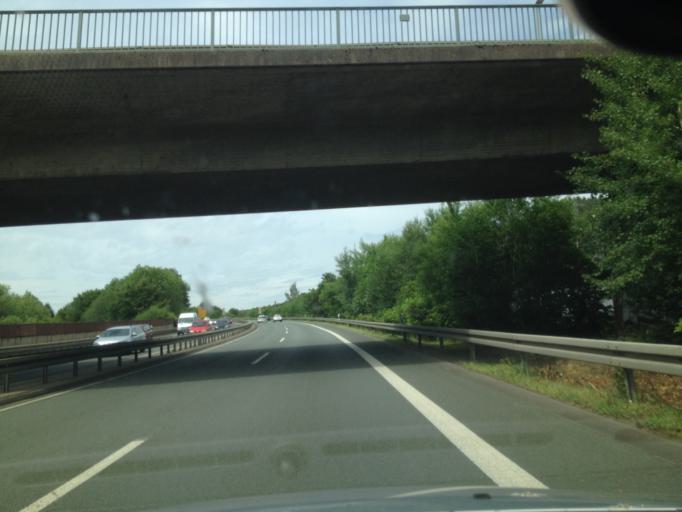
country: DE
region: North Rhine-Westphalia
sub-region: Regierungsbezirk Arnsberg
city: Siegen
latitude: 50.9238
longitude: 8.0152
